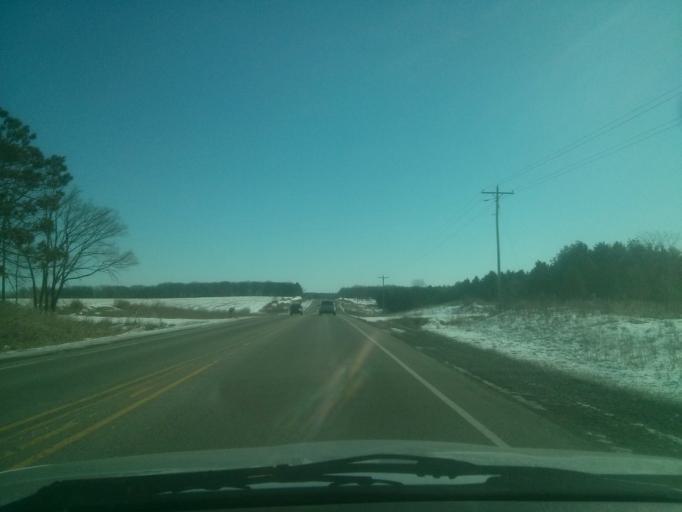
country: US
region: Wisconsin
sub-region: Saint Croix County
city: New Richmond
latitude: 45.1368
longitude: -92.4337
